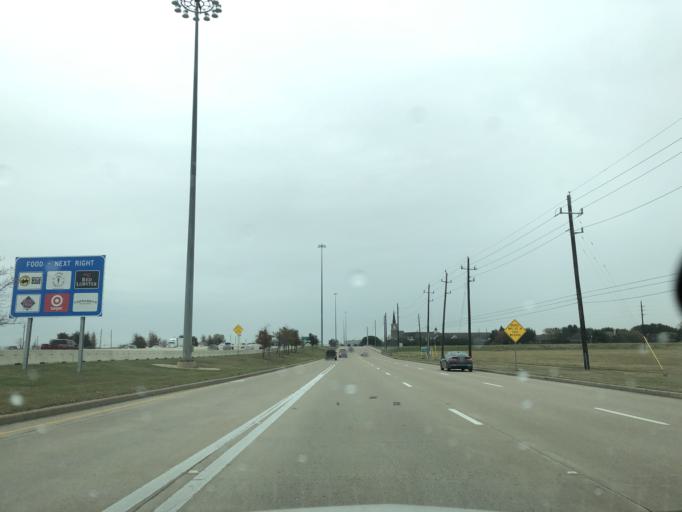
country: US
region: Texas
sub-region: Fort Bend County
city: Sugar Land
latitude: 29.5836
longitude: -95.6430
